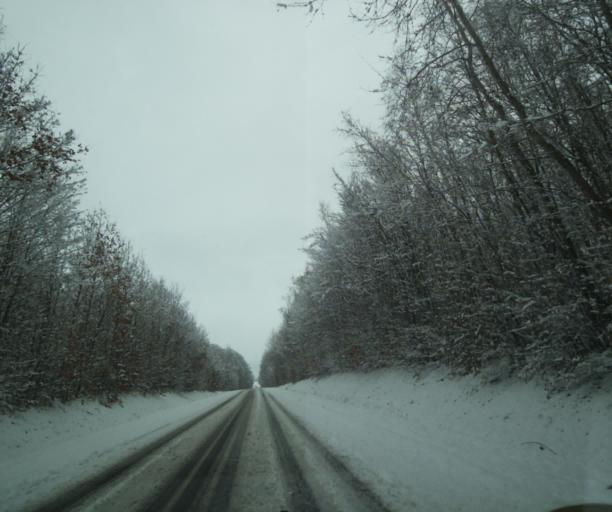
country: FR
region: Champagne-Ardenne
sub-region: Departement de la Haute-Marne
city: Montier-en-Der
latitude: 48.5286
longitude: 4.7920
